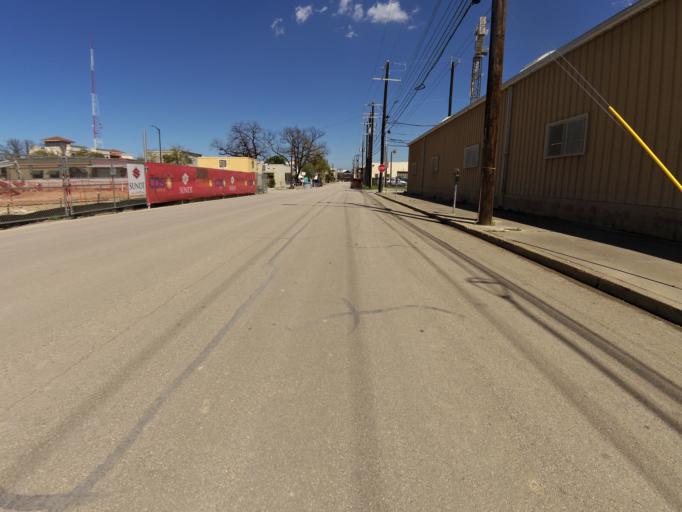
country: US
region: Texas
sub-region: Bexar County
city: San Antonio
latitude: 29.4323
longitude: -98.4846
